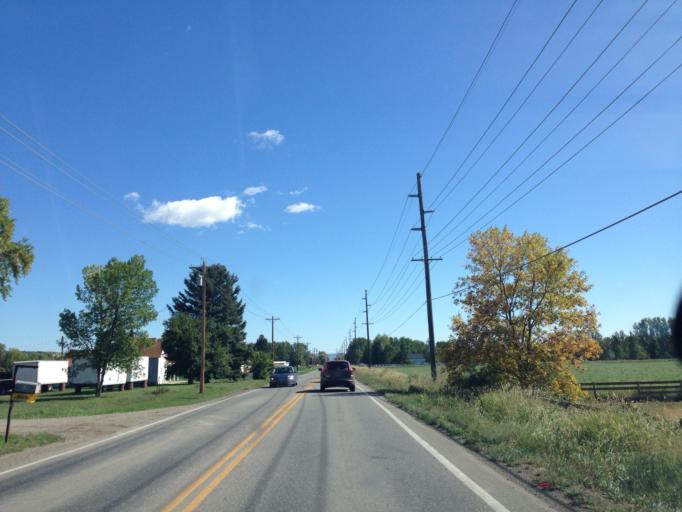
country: US
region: Montana
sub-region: Yellowstone County
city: Billings
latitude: 45.7841
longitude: -108.6367
